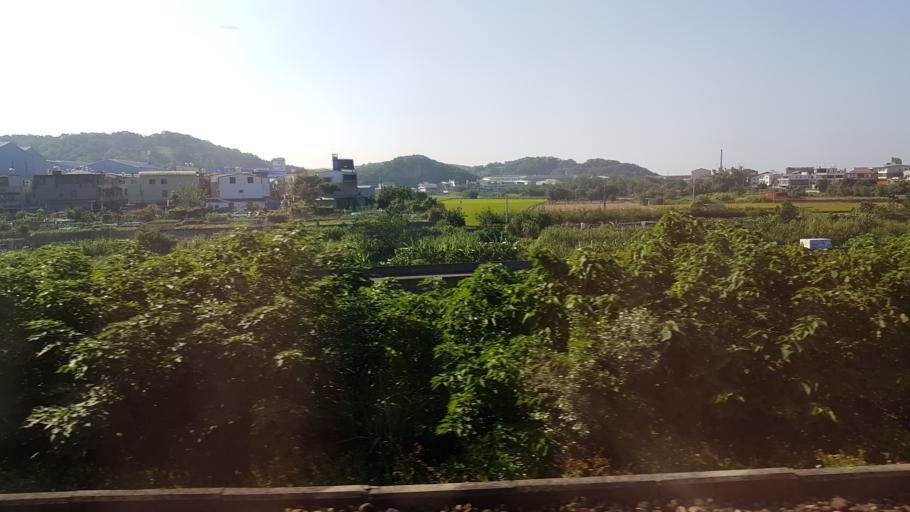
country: TW
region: Taiwan
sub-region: Miaoli
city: Miaoli
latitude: 24.6502
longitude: 120.8760
